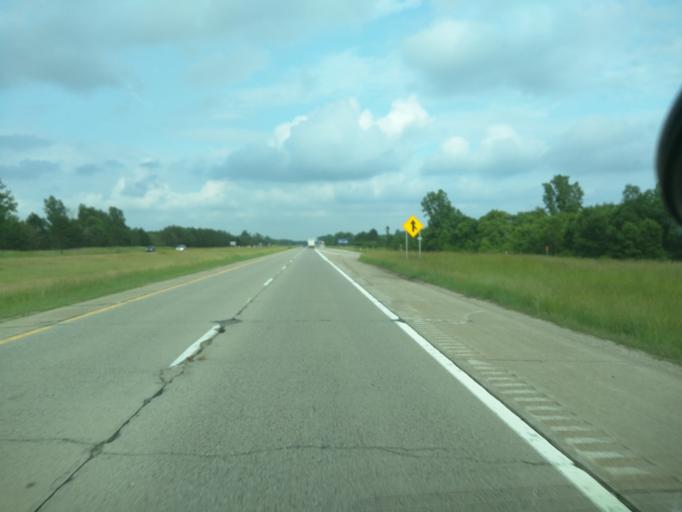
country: US
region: Michigan
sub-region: Clinton County
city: DeWitt
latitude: 42.8165
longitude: -84.5675
